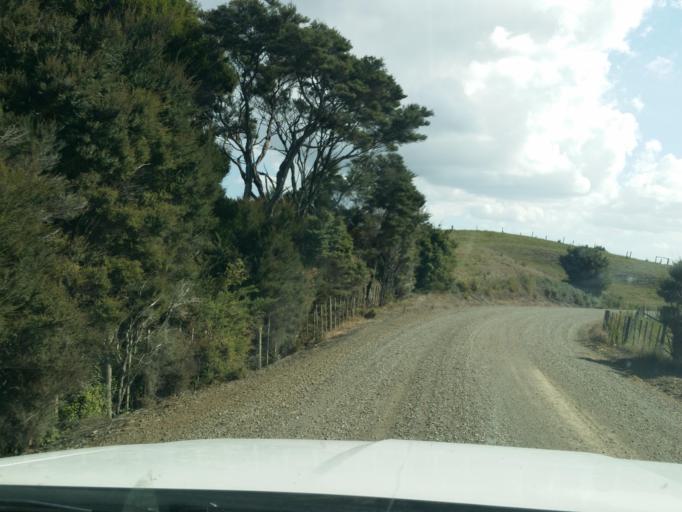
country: NZ
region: Auckland
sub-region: Auckland
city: Wellsford
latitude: -36.1616
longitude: 174.5325
